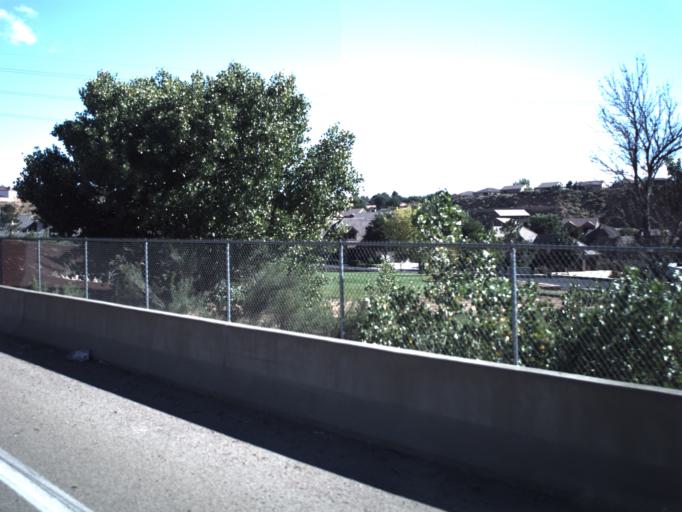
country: US
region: Utah
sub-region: Washington County
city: LaVerkin
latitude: 37.2195
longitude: -113.2759
